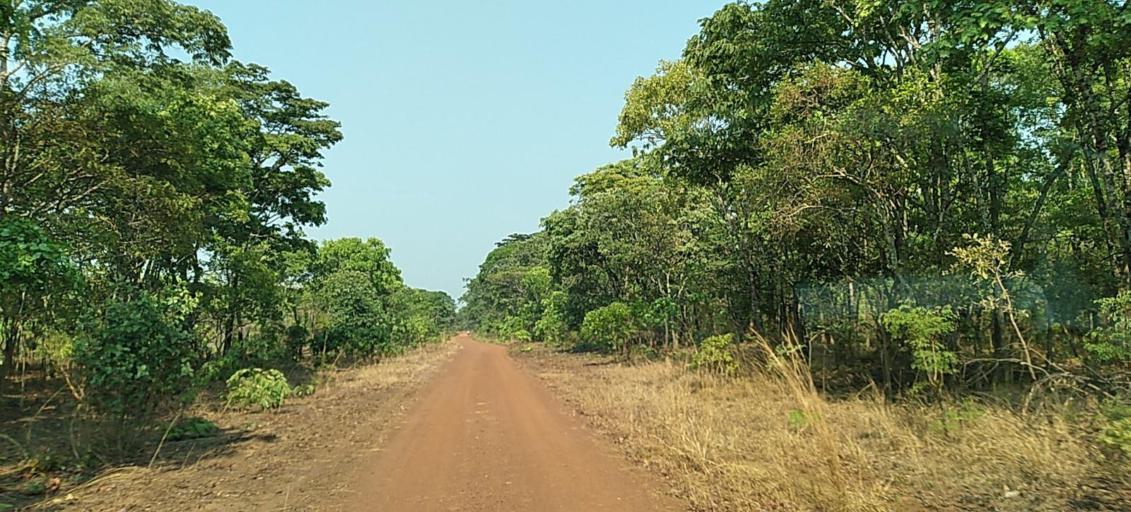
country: ZM
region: Copperbelt
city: Chingola
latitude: -12.8801
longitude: 27.4368
